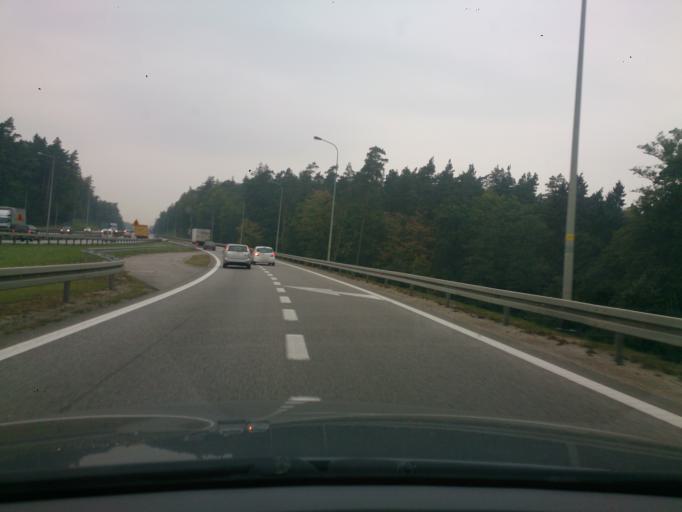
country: PL
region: Pomeranian Voivodeship
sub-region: Sopot
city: Sopot
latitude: 54.3794
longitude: 18.5118
